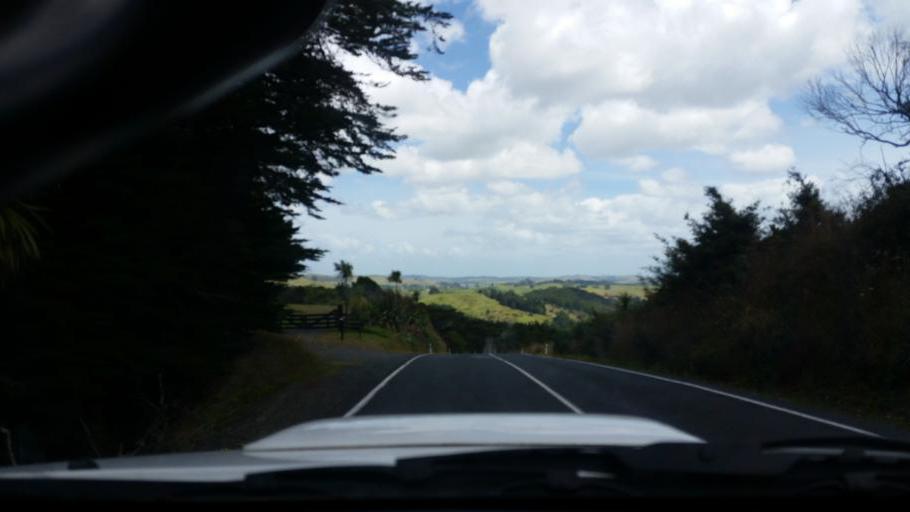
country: NZ
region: Northland
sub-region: Whangarei
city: Ruakaka
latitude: -36.0876
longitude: 174.2397
